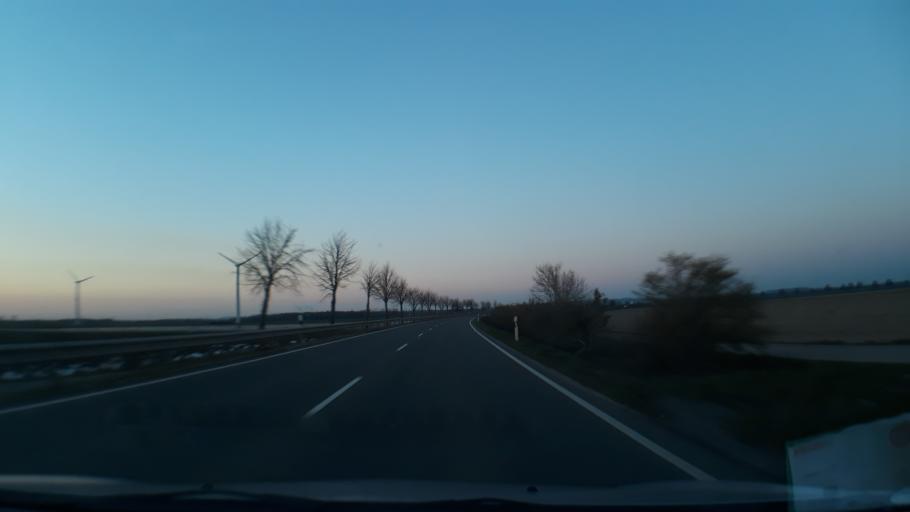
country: DE
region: North Rhine-Westphalia
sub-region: Regierungsbezirk Koln
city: Norvenich
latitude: 50.8565
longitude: 6.6139
